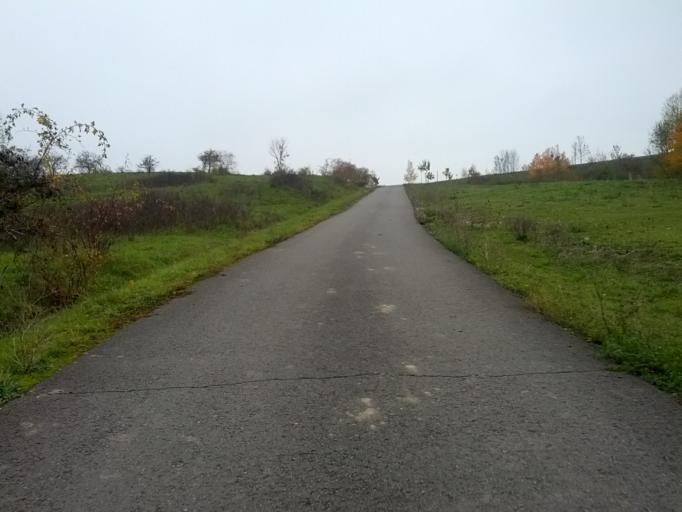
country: DE
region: Thuringia
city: Thal
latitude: 50.9657
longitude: 10.3787
